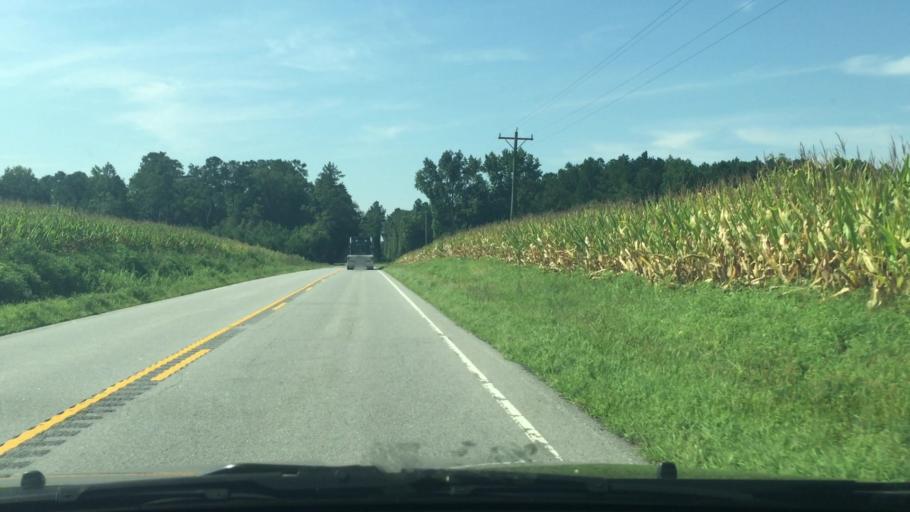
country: US
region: Virginia
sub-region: Sussex County
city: Sussex
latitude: 36.8974
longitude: -77.1520
